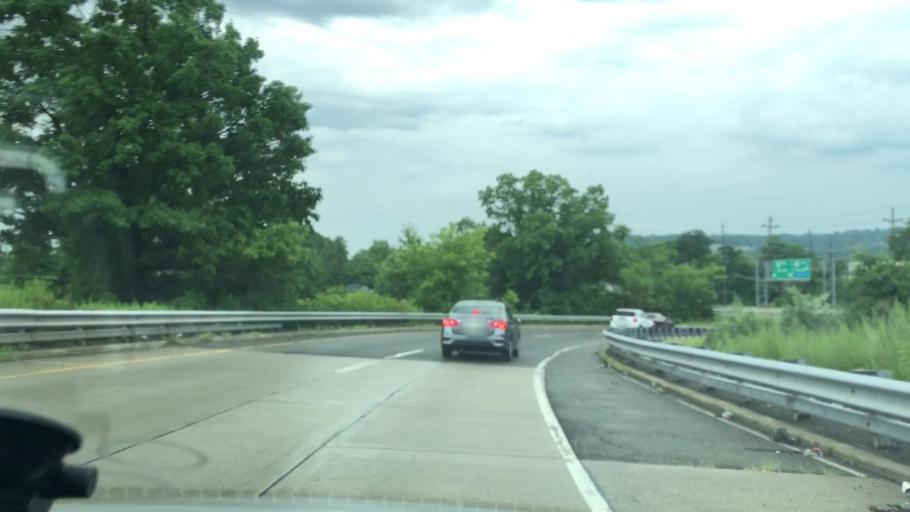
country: US
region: New Jersey
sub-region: Passaic County
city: Singac
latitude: 40.8953
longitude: -74.2517
